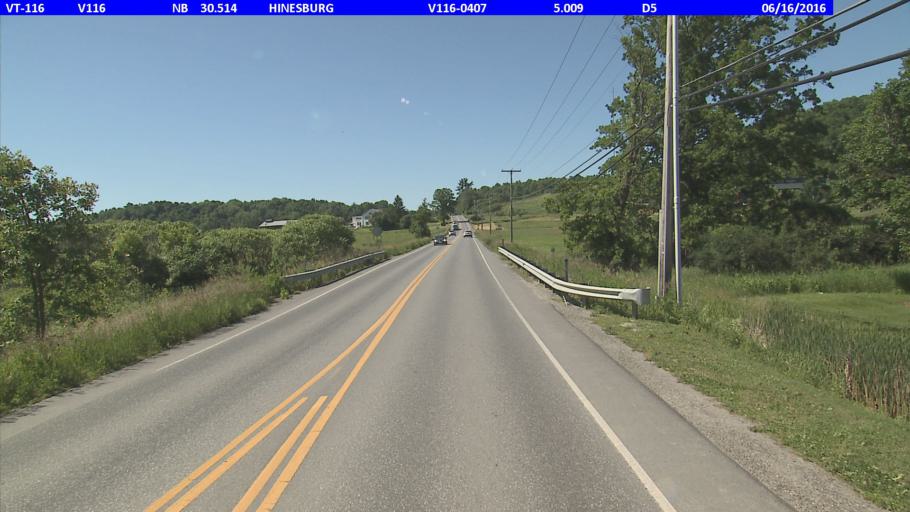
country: US
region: Vermont
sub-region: Chittenden County
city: Hinesburg
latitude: 44.3353
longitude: -73.1128
